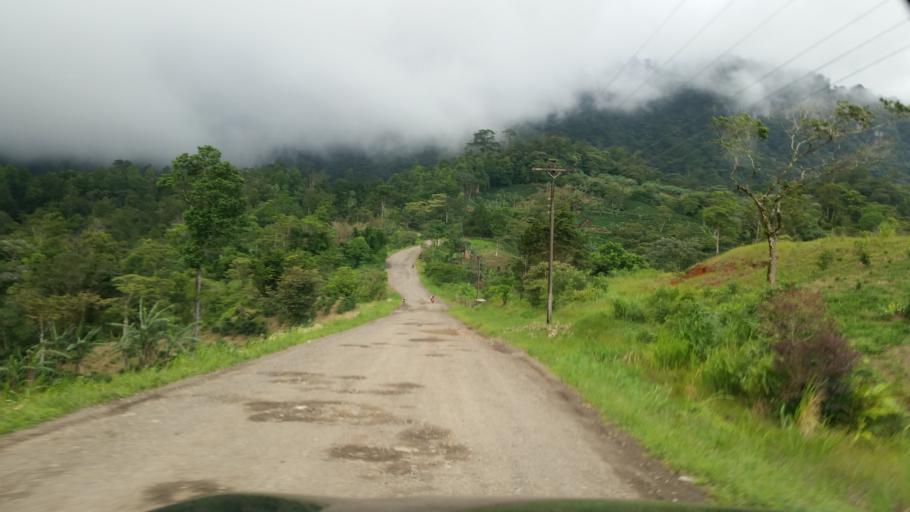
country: NI
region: Jinotega
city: San Jose de Bocay
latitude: 13.2802
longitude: -85.7250
